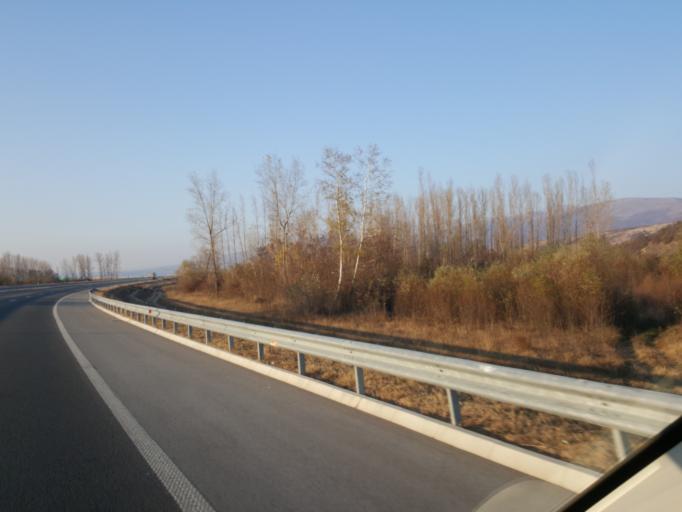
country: RS
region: Central Serbia
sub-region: Pirotski Okrug
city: Dimitrovgrad
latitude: 43.0632
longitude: 22.6814
